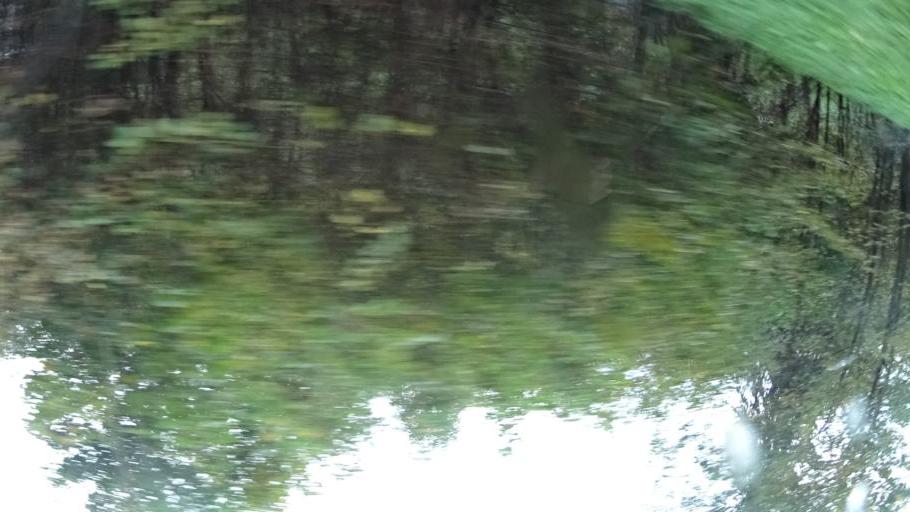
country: DE
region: Baden-Wuerttemberg
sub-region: Karlsruhe Region
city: Eberbach
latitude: 49.5005
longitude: 9.0437
